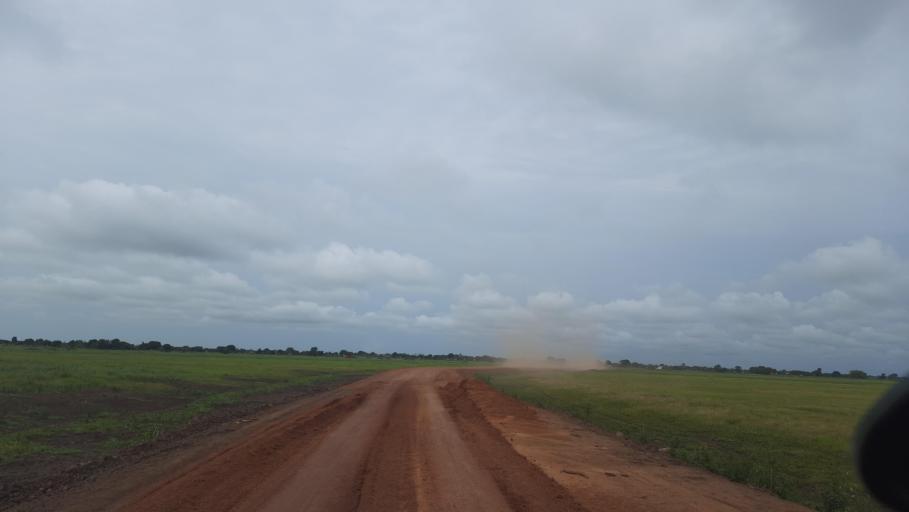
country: ET
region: Gambela
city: Gambela
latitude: 8.3373
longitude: 33.7763
